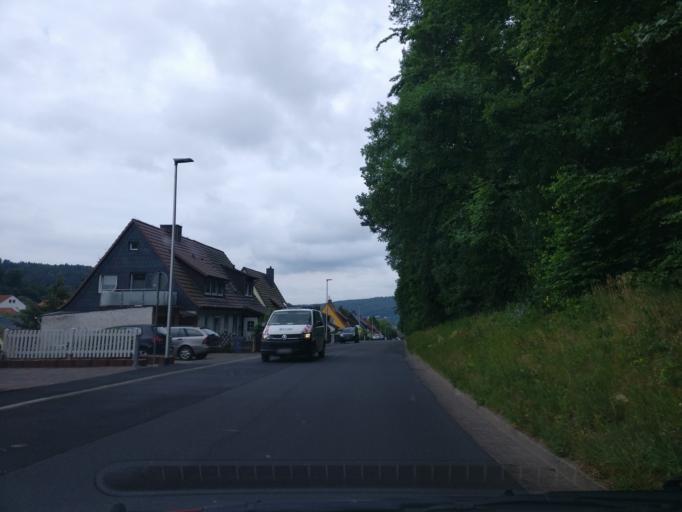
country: DE
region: Lower Saxony
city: Hannoversch Munden
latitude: 51.4188
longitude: 9.6872
